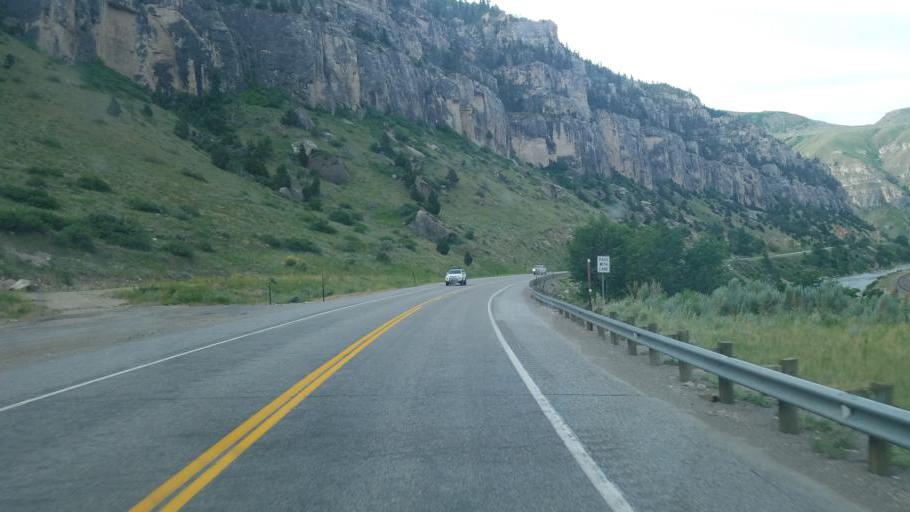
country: US
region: Wyoming
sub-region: Hot Springs County
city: Thermopolis
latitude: 43.5258
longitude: -108.1750
